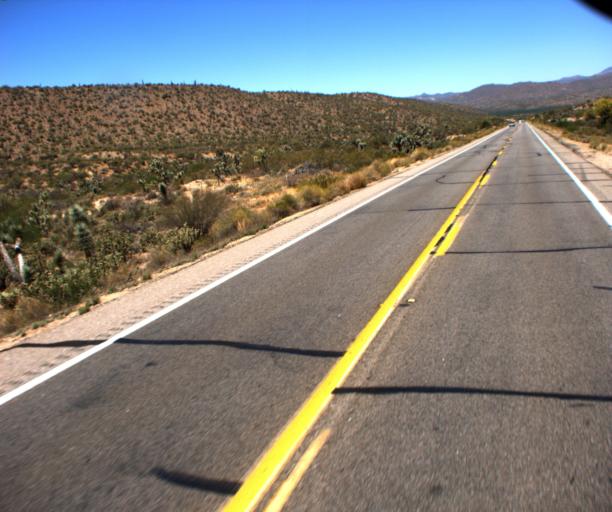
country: US
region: Arizona
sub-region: Yavapai County
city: Bagdad
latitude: 34.3500
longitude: -113.1636
